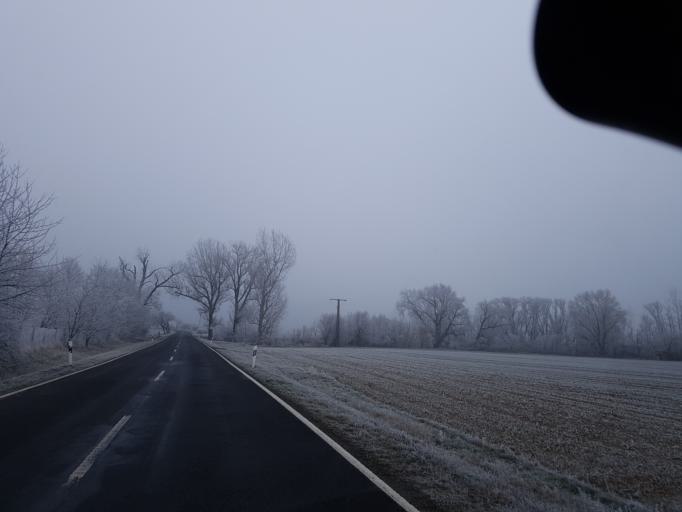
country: DE
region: Brandenburg
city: Muhlberg
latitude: 51.4290
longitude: 13.2379
